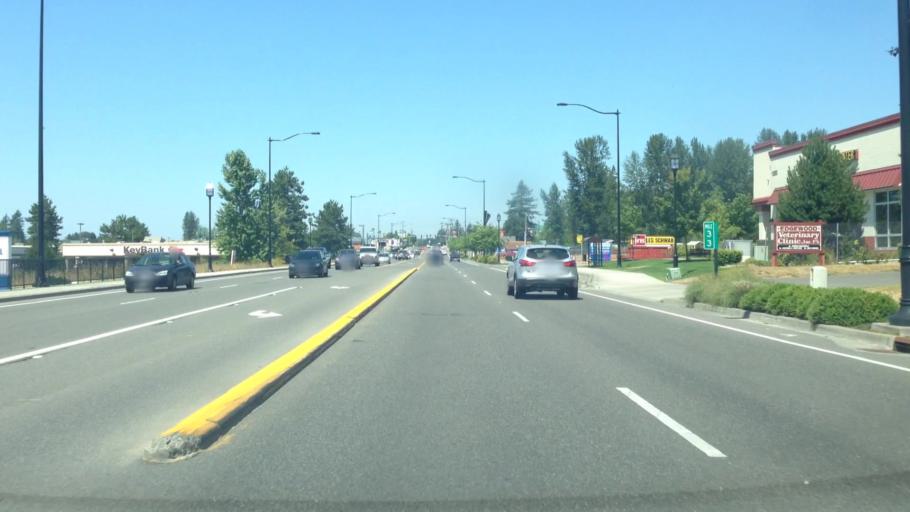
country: US
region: Washington
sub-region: Pierce County
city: Edgewood
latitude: 47.2451
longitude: -122.2939
